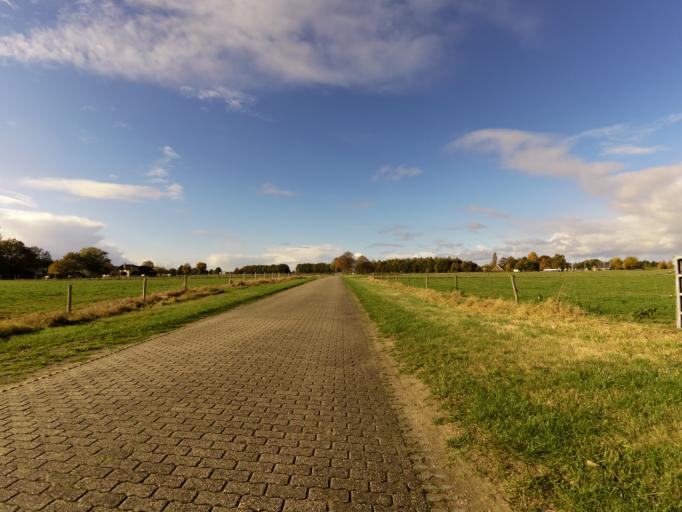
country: NL
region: Gelderland
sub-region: Gemeente Doesburg
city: Doesburg
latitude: 51.9599
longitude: 6.1957
